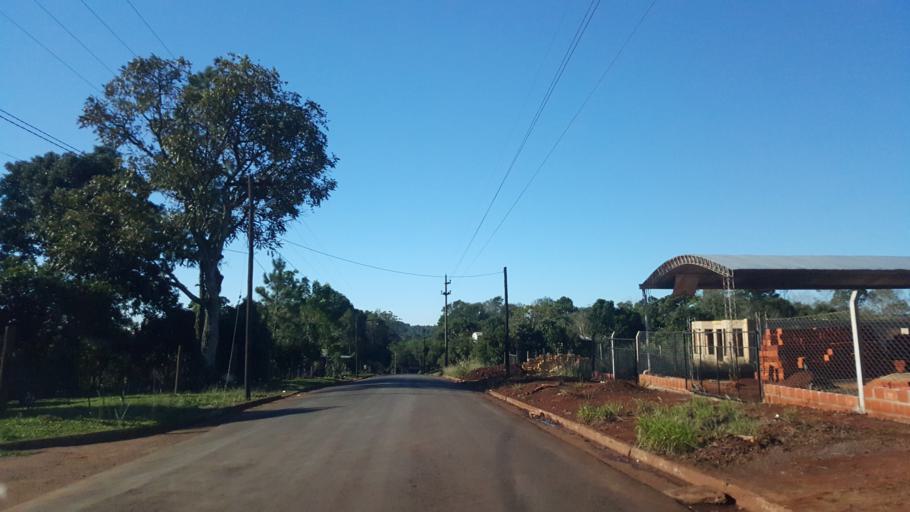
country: AR
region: Misiones
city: Gobernador Roca
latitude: -27.1813
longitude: -55.4577
